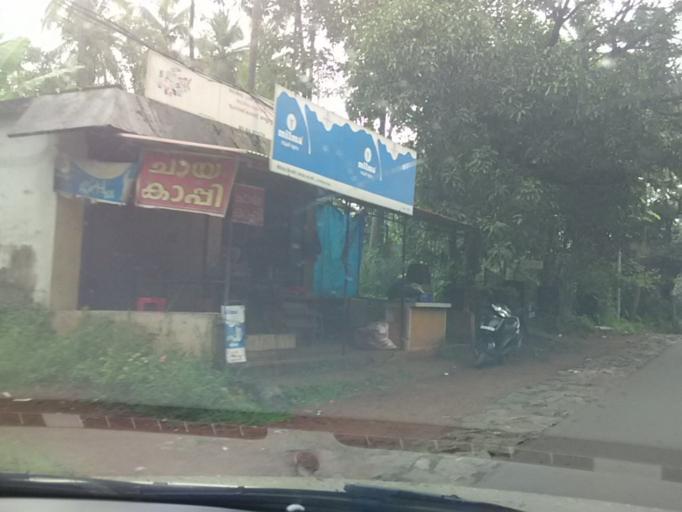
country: IN
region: Kerala
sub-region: Kozhikode
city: Kunnamangalam
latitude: 11.3084
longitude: 75.9069
